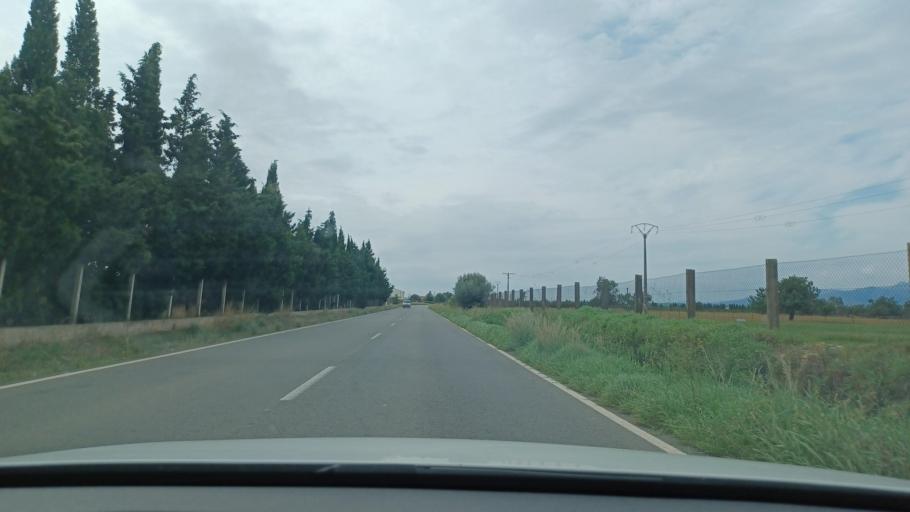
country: ES
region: Catalonia
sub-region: Provincia de Tarragona
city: Tortosa
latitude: 40.7691
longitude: 0.5098
